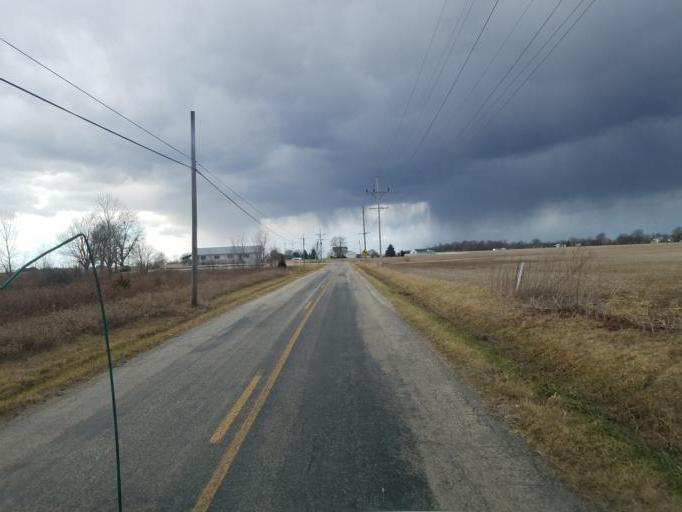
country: US
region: Ohio
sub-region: Marion County
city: Prospect
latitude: 40.4589
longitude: -83.0998
